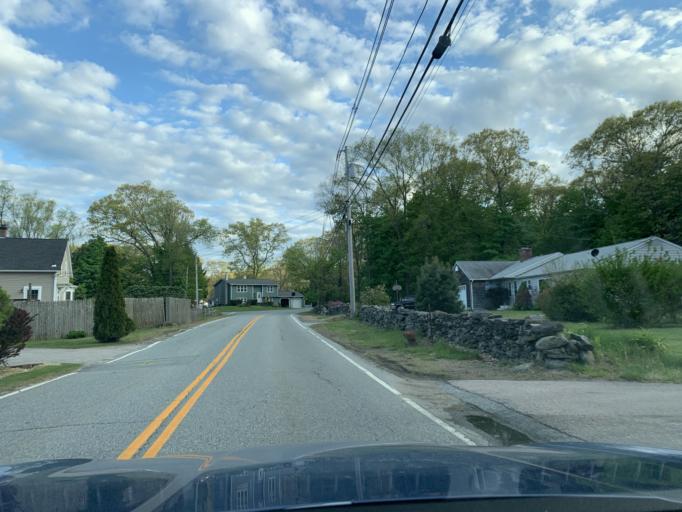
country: US
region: Rhode Island
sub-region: Kent County
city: East Greenwich
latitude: 41.6322
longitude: -71.4592
